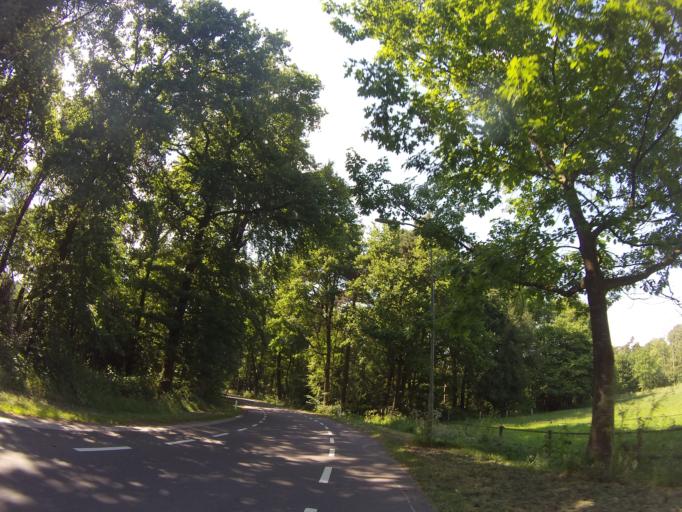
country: NL
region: Gelderland
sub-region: Gemeente Barneveld
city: Barneveld
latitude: 52.1460
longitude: 5.5502
